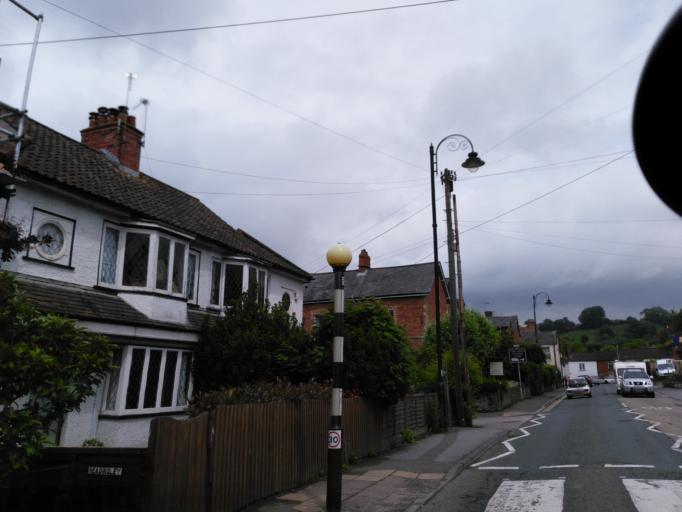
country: GB
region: England
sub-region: Somerset
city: Glastonbury
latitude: 51.1443
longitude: -2.7190
